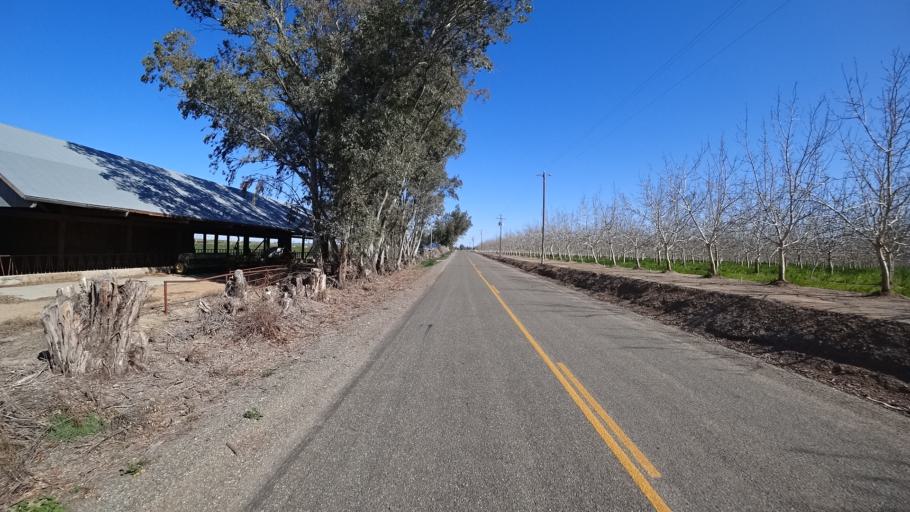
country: US
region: California
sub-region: Glenn County
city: Orland
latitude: 39.7378
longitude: -122.2482
